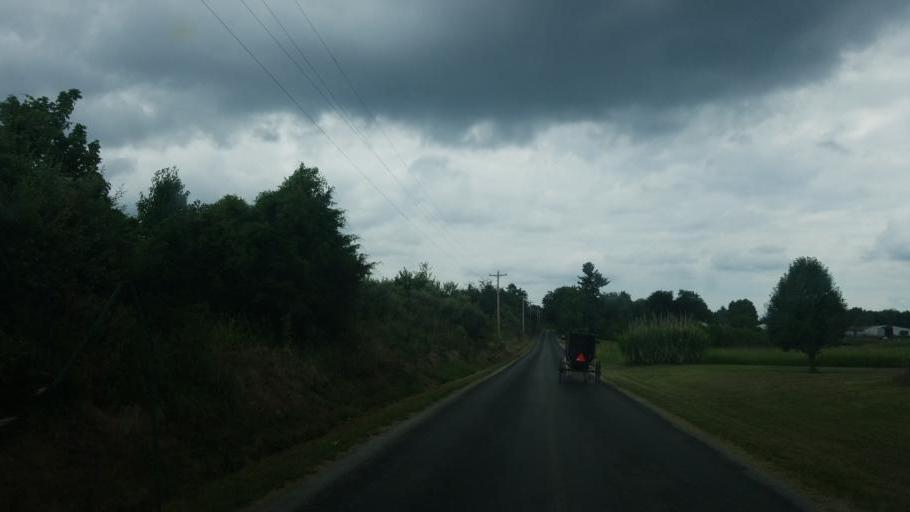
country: US
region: Illinois
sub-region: Jackson County
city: Murphysboro
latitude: 37.7090
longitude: -89.3316
